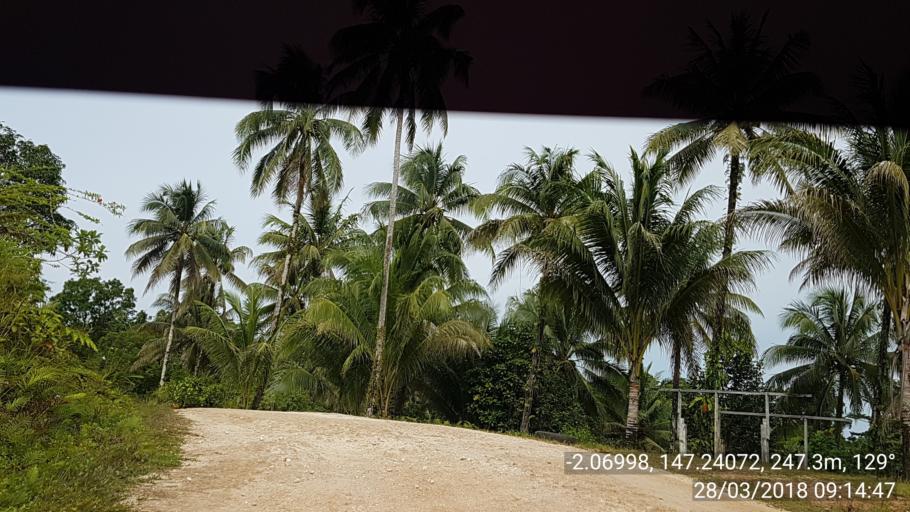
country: PG
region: Manus
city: Lorengau
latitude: -2.0700
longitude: 147.2408
